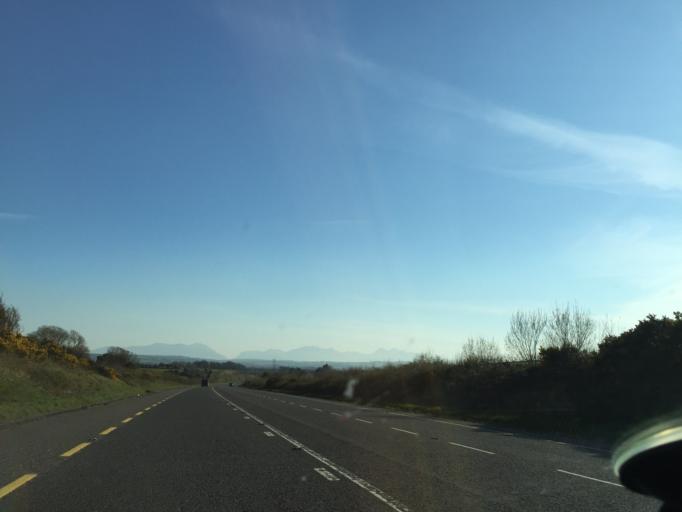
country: IE
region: Munster
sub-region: Ciarrai
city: Castleisland
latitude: 52.2119
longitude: -9.5656
